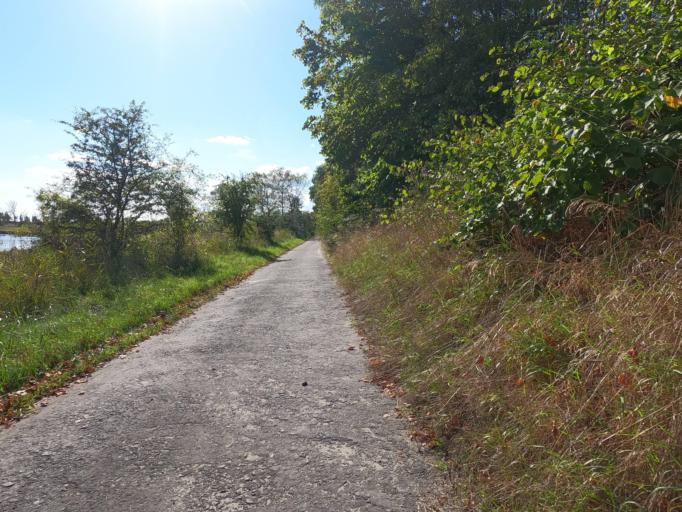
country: DE
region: Schleswig-Holstein
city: Grossenbrode
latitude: 54.3925
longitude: 11.1070
